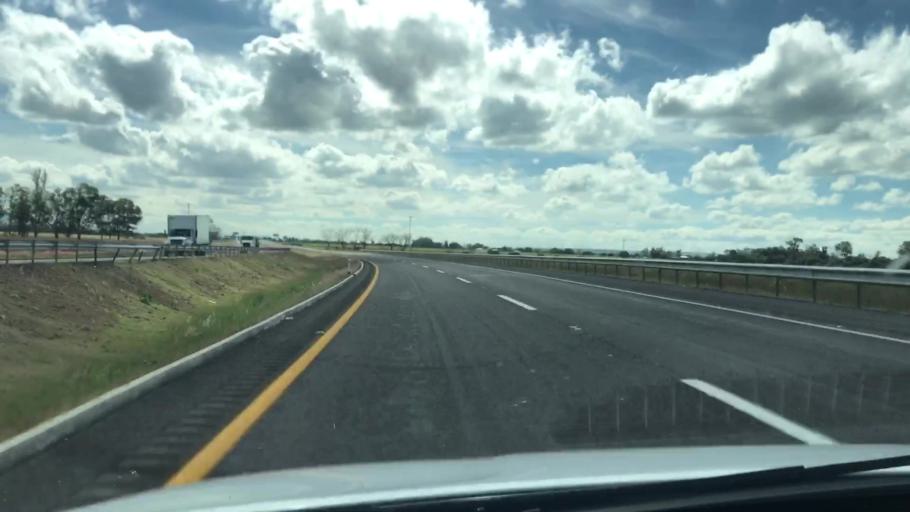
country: MX
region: Guanajuato
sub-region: Leon
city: San Antonio de los Tepetates
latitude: 21.0220
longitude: -101.6114
